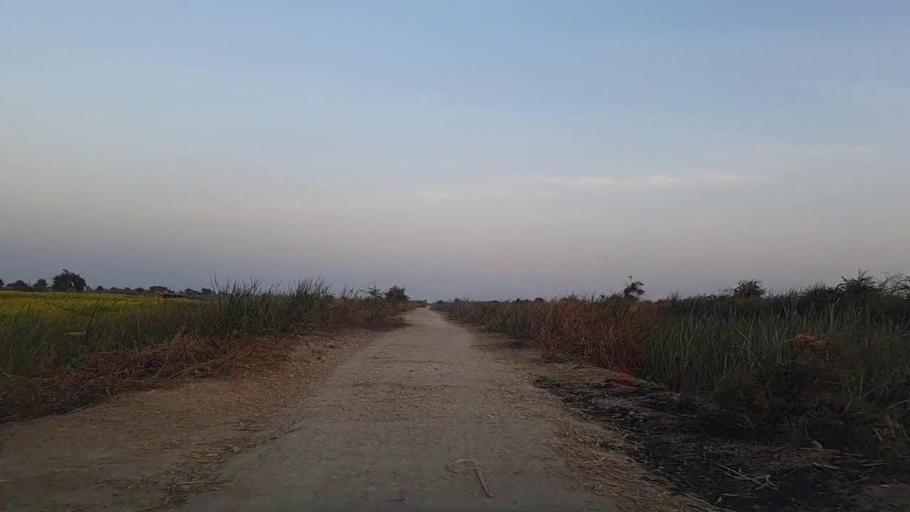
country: PK
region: Sindh
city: Tando Mittha Khan
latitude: 25.9448
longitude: 69.1265
